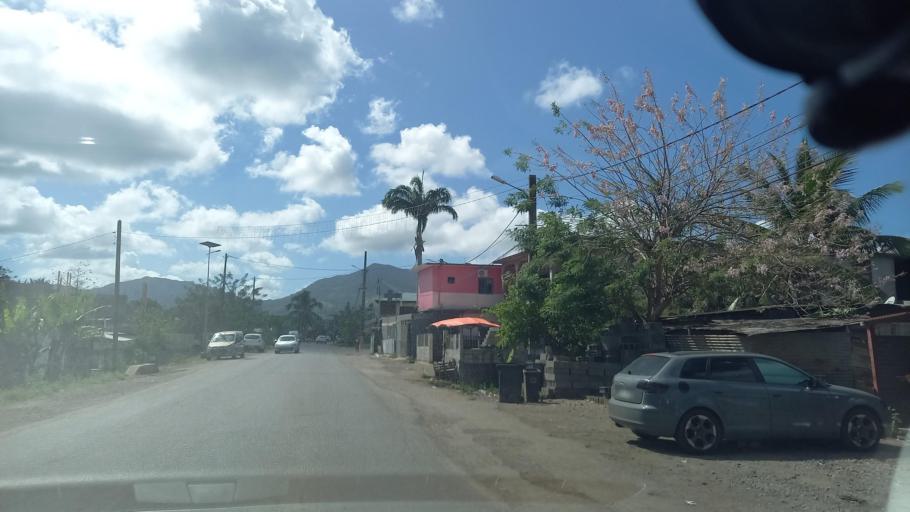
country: YT
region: Chirongui
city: Chirongui
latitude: -12.9305
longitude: 45.1528
